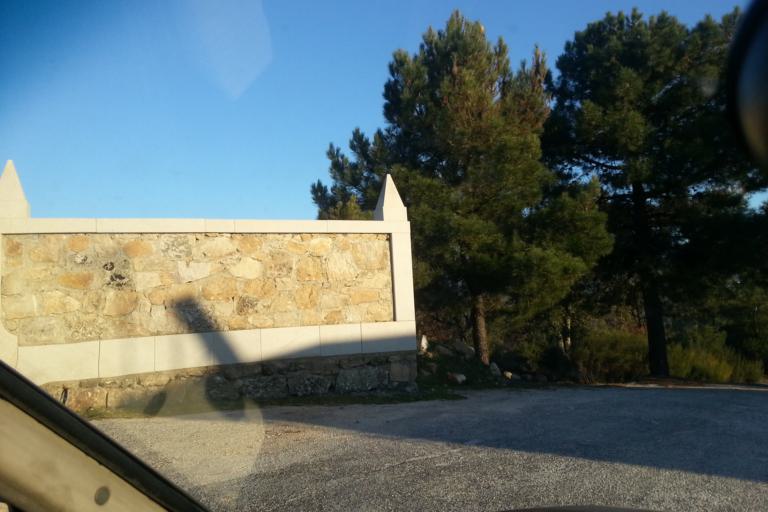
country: PT
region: Guarda
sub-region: Fornos de Algodres
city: Fornos de Algodres
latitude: 40.6078
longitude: -7.5004
